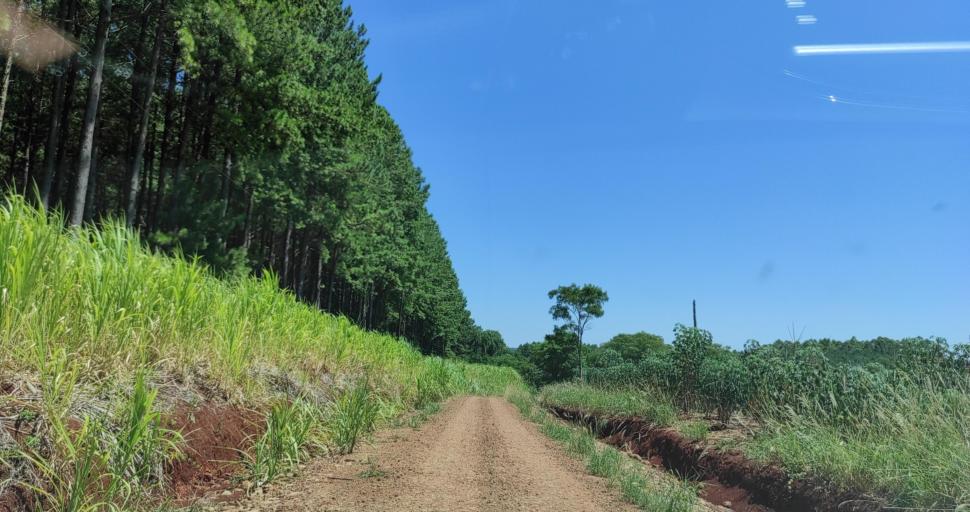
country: AR
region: Misiones
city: Capiovi
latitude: -26.9251
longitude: -55.0970
